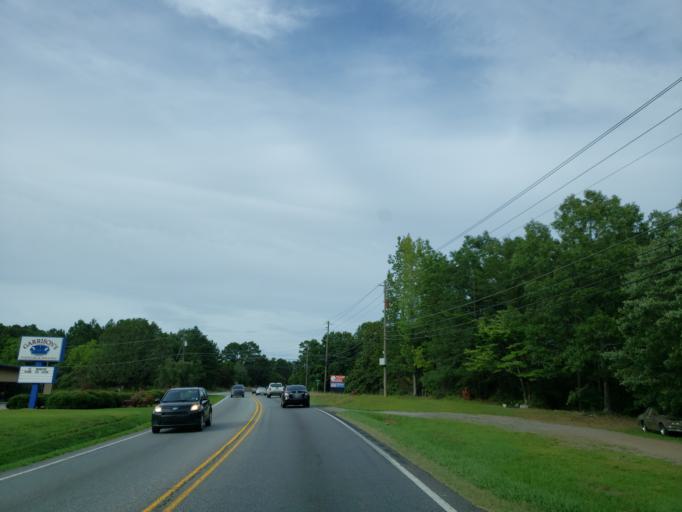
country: US
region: Georgia
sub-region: Cherokee County
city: Canton
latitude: 34.2387
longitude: -84.4305
